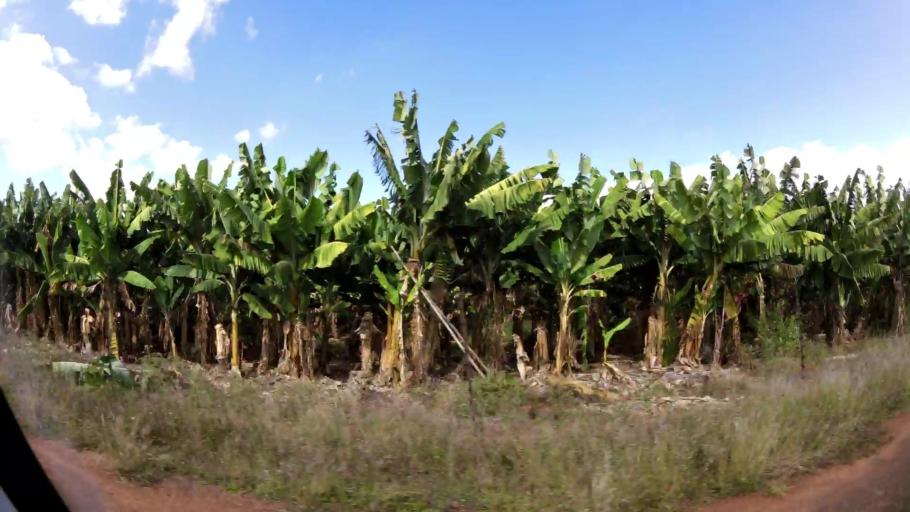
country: ZA
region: Limpopo
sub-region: Mopani District Municipality
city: Tzaneen
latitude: -23.7958
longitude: 30.1403
